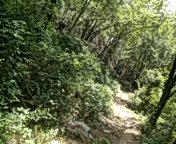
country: IT
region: Tuscany
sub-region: Provincia di Lucca
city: Pontestazzemese
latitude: 43.9969
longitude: 10.3322
